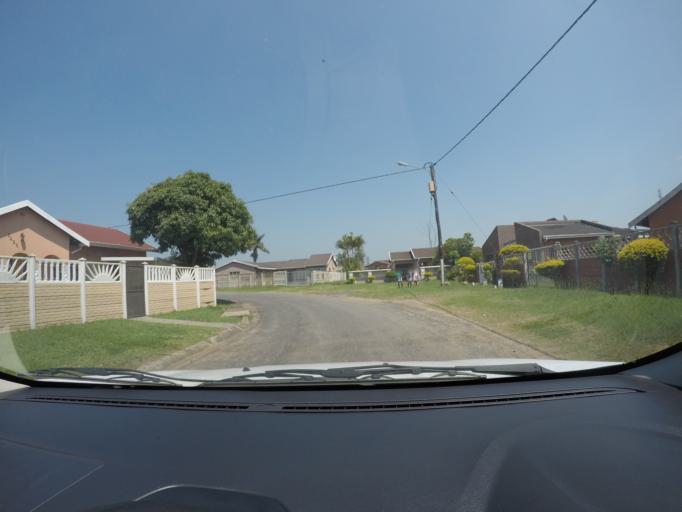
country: ZA
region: KwaZulu-Natal
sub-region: uThungulu District Municipality
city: eSikhawini
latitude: -28.8628
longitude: 31.9215
